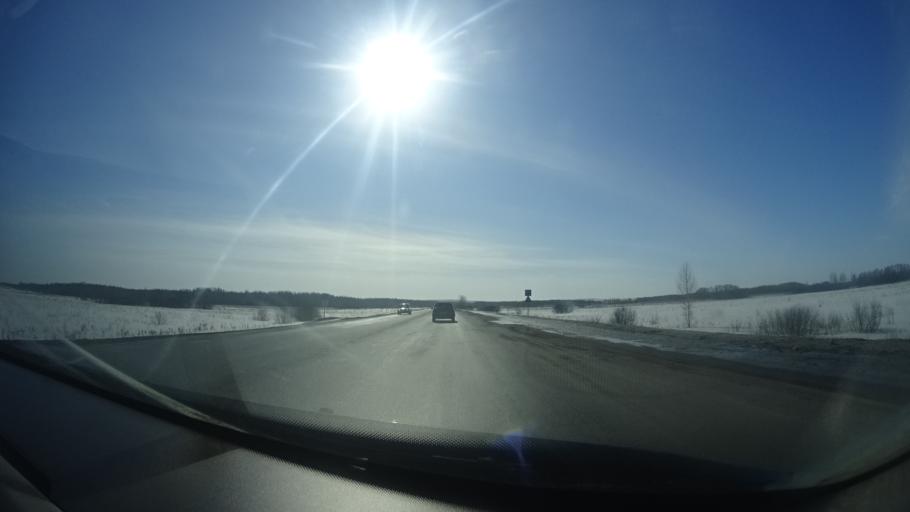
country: RU
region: Bashkortostan
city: Mikhaylovka
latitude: 54.9226
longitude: 55.7373
